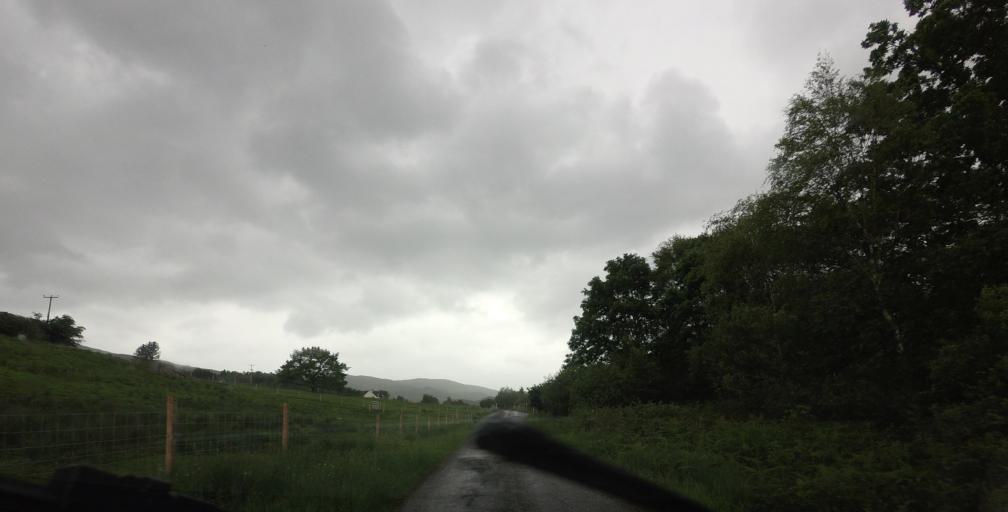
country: GB
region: Scotland
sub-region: Argyll and Bute
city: Oban
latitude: 56.7130
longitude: -5.5626
